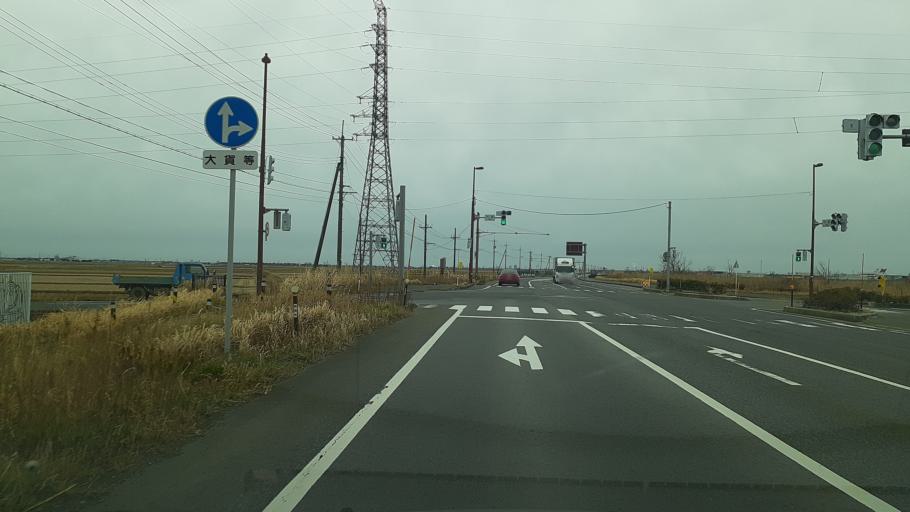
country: JP
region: Niigata
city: Niitsu-honcho
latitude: 37.8027
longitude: 139.1027
